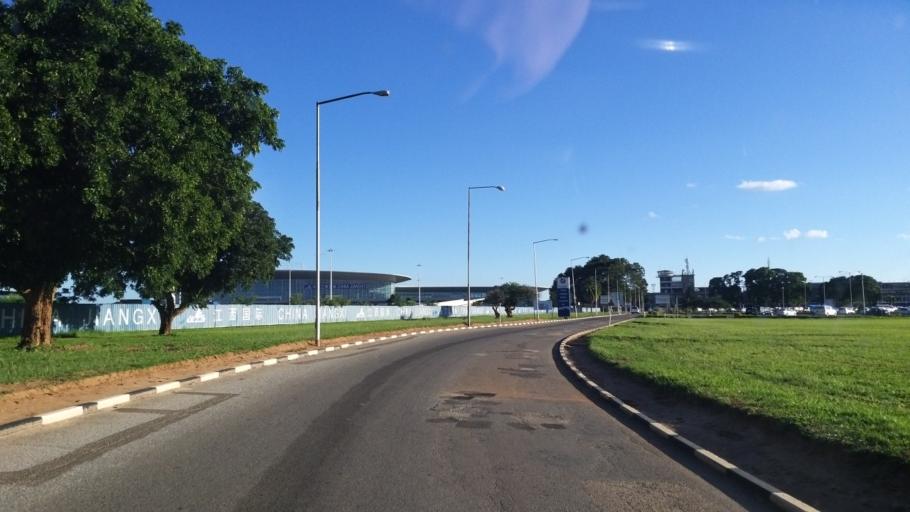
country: ZM
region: Lusaka
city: Lusaka
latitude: -15.3214
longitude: 28.4473
